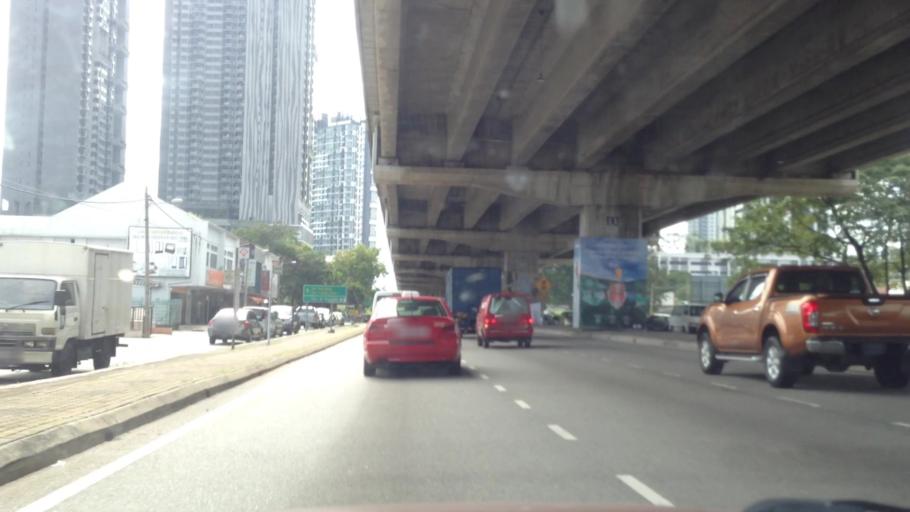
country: MY
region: Selangor
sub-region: Petaling
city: Petaling Jaya
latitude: 3.0823
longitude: 101.6583
